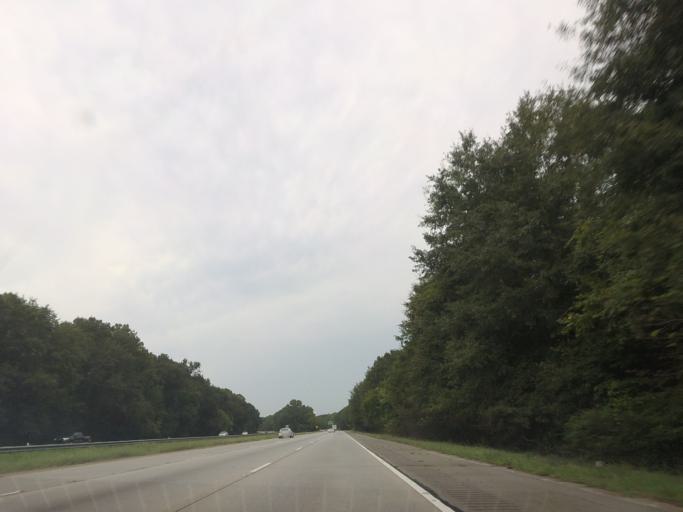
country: US
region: Georgia
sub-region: Bibb County
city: Macon
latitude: 32.7691
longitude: -83.6978
